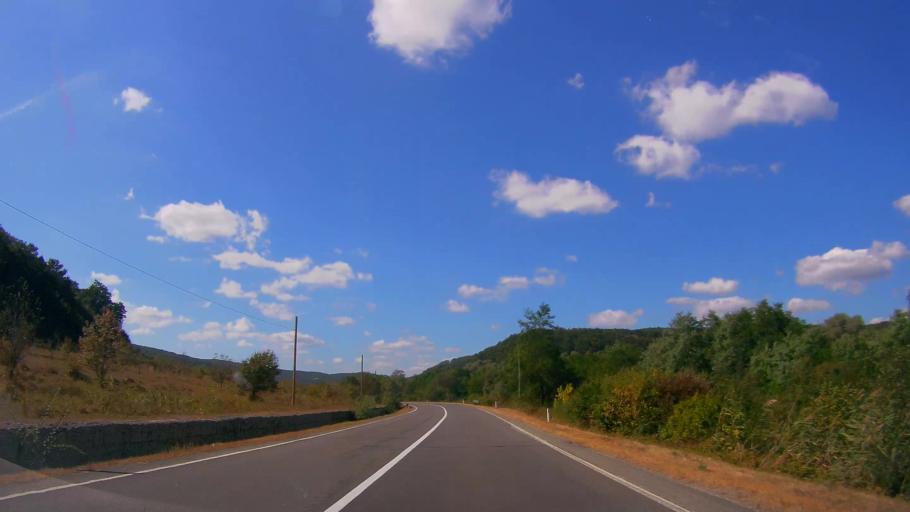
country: RO
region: Salaj
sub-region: Comuna Zimbor
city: Zimbor
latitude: 46.9675
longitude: 23.2863
